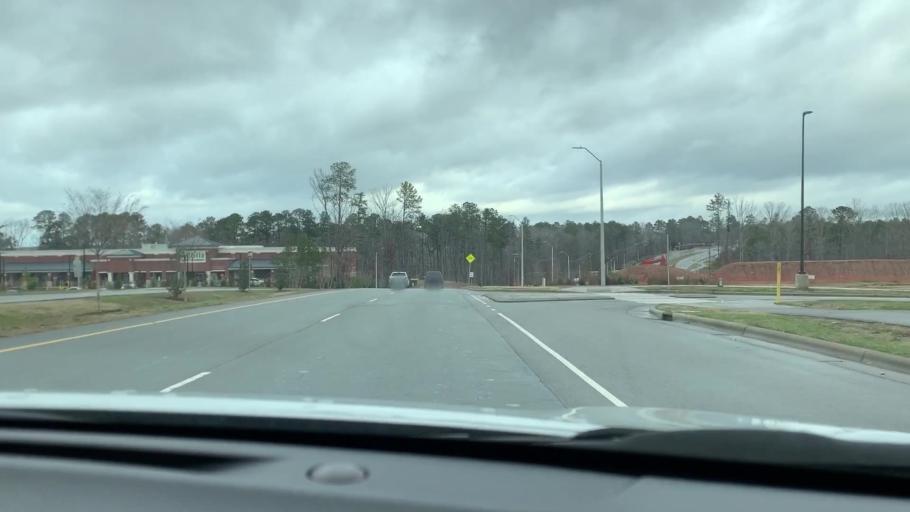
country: US
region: North Carolina
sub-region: Wake County
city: Green Level
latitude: 35.8234
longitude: -78.9021
